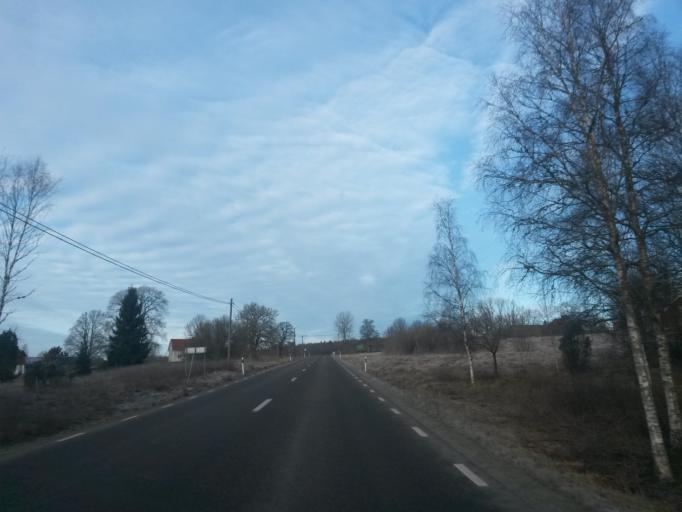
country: SE
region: Vaestra Goetaland
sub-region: Boras Kommun
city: Boras
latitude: 57.8326
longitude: 12.9930
